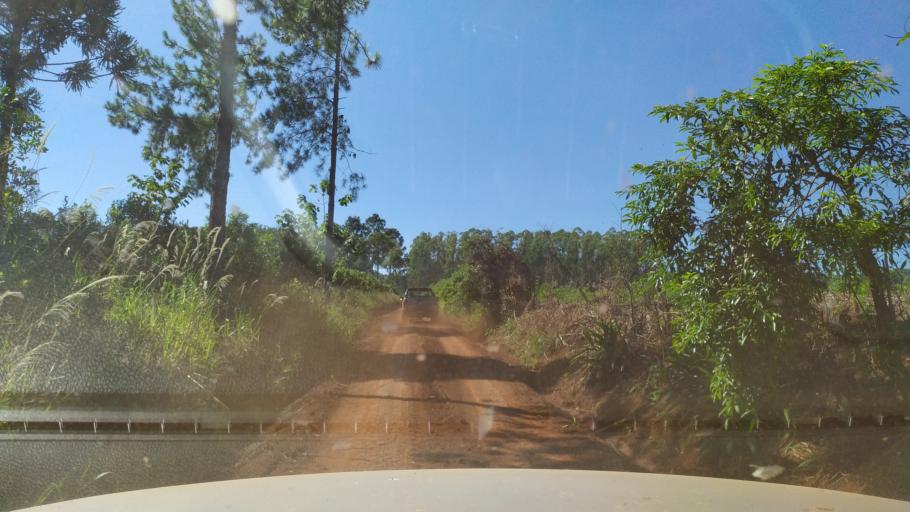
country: AR
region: Misiones
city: Caraguatay
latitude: -26.6702
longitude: -54.6985
